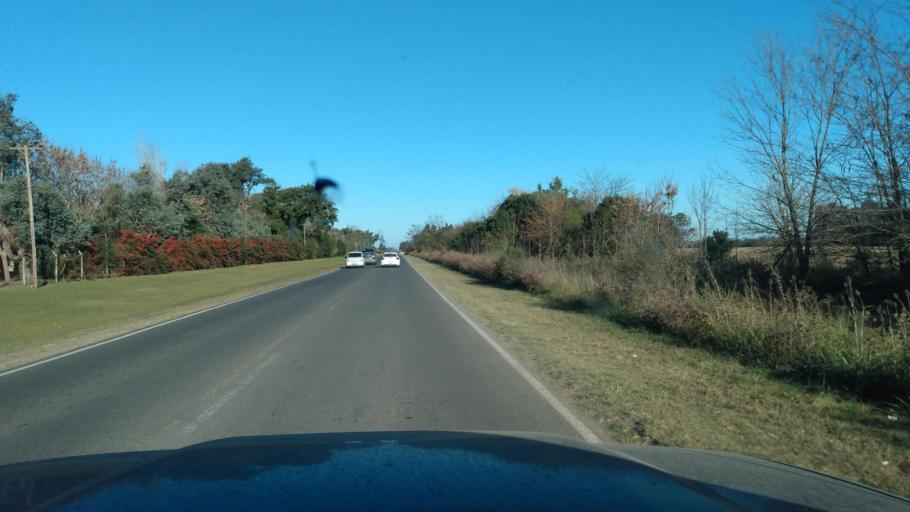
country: AR
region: Buenos Aires
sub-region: Partido de Lujan
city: Lujan
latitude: -34.5147
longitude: -59.1803
